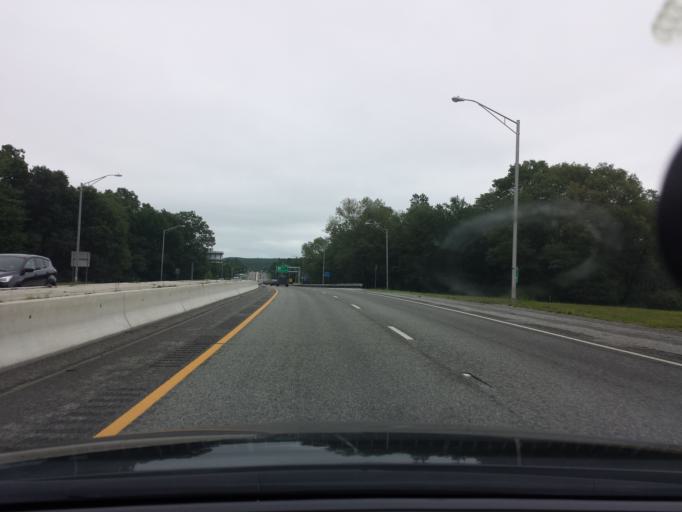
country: US
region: Rhode Island
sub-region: Washington County
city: Hope Valley
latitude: 41.5108
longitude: -71.6933
